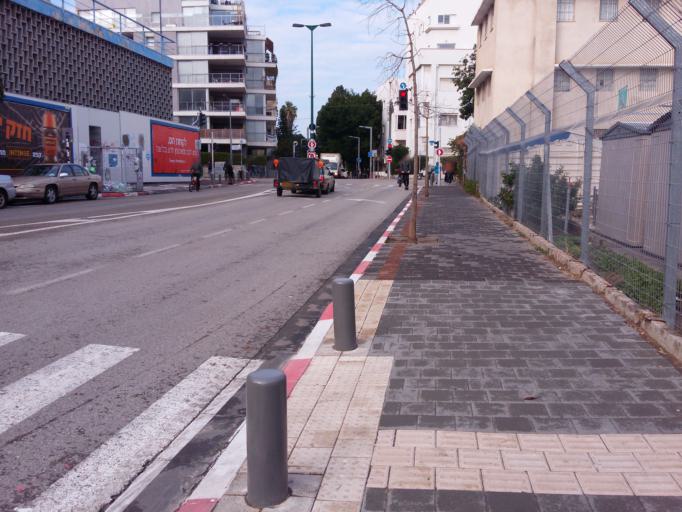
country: IL
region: Tel Aviv
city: Tel Aviv
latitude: 32.0674
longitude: 34.7806
